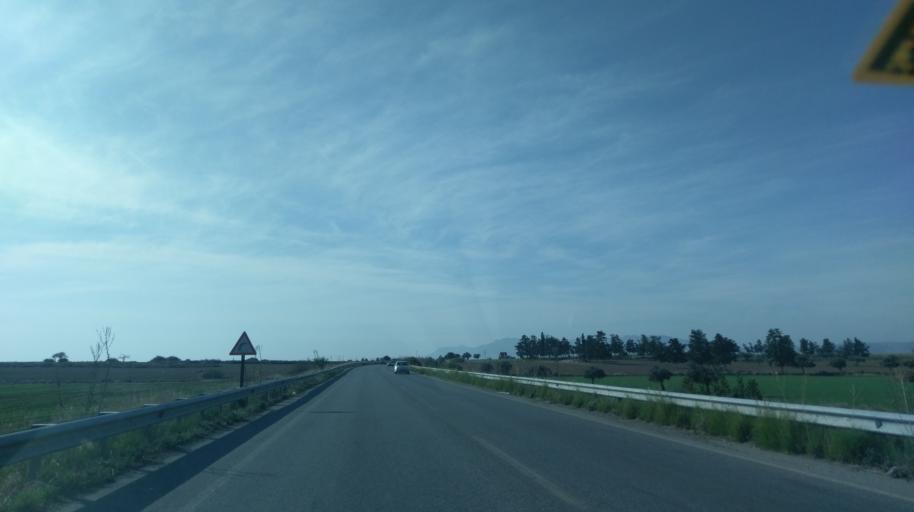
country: CY
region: Ammochostos
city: Lefkonoiko
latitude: 35.2612
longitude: 33.7635
